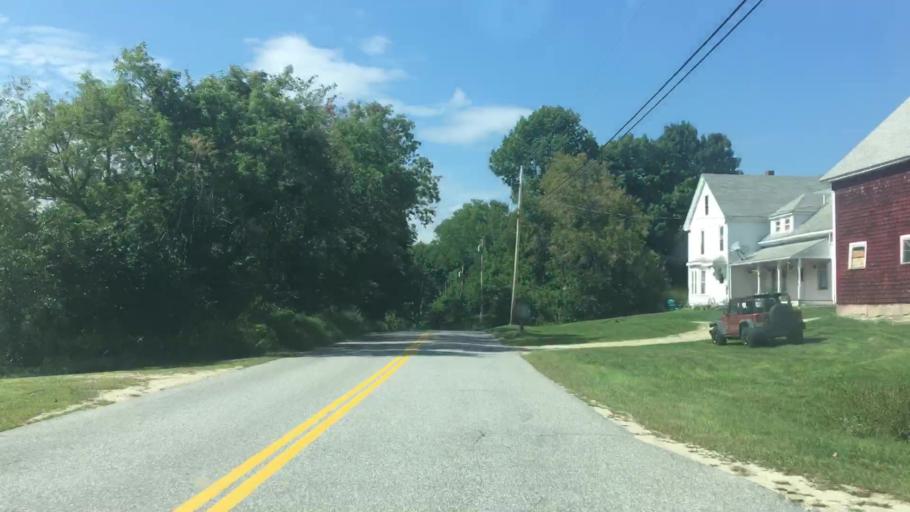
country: US
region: Maine
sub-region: Androscoggin County
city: Poland
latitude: 44.0066
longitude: -70.3741
